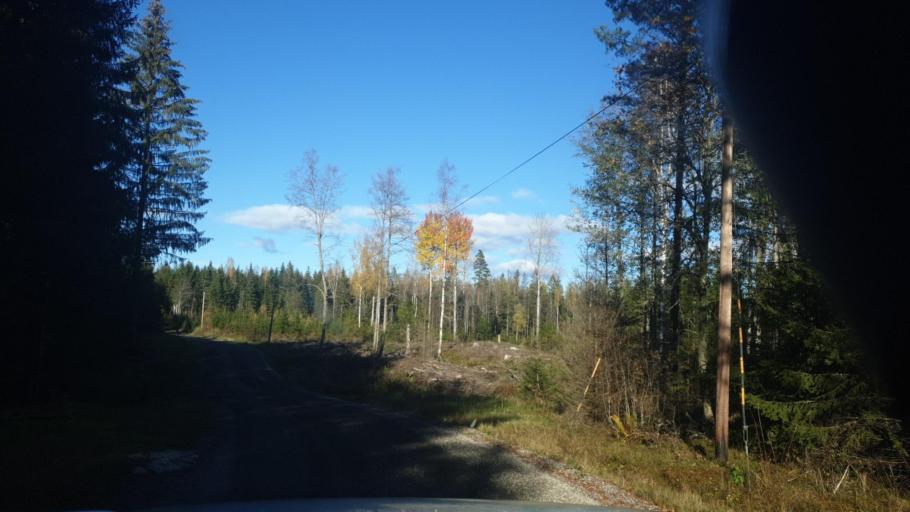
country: SE
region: Vaermland
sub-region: Arvika Kommun
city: Arvika
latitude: 59.5555
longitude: 12.8479
